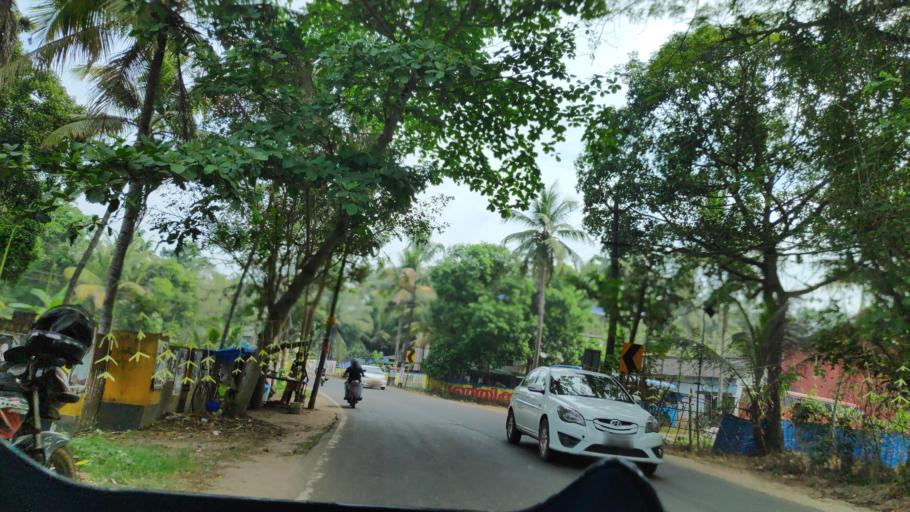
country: IN
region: Kerala
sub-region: Alappuzha
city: Vayalar
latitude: 9.7123
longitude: 76.3586
